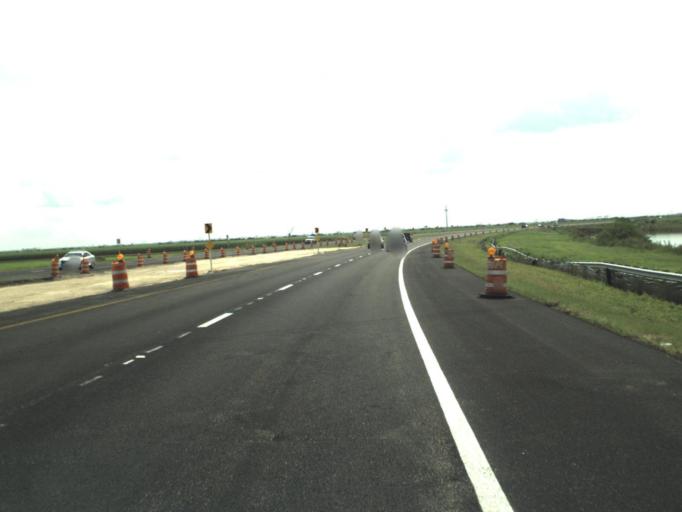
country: US
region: Florida
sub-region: Palm Beach County
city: Loxahatchee Groves
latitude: 26.7254
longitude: -80.4457
